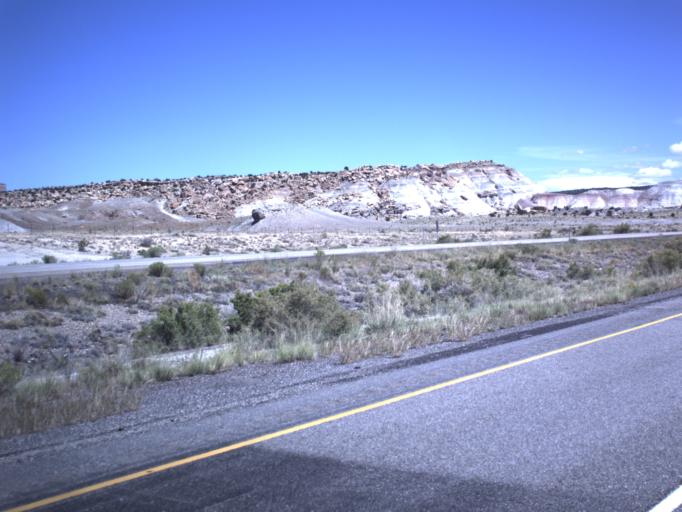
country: US
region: Utah
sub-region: Emery County
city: Ferron
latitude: 38.8161
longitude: -111.1844
